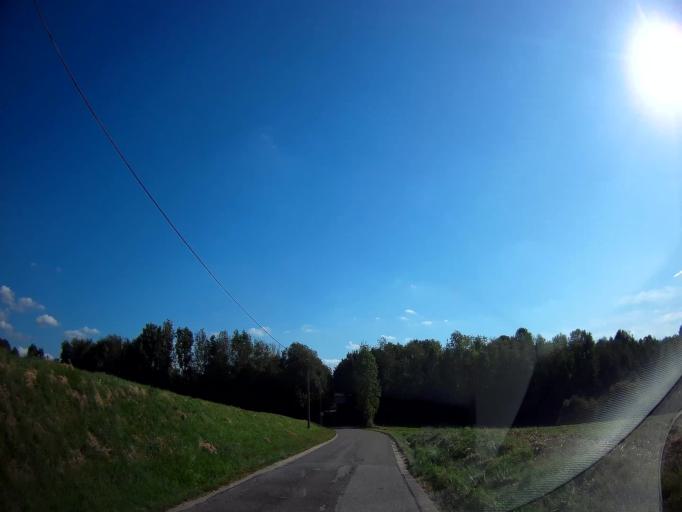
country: BE
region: Wallonia
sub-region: Province de Namur
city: Houyet
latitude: 50.2428
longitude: 4.9867
